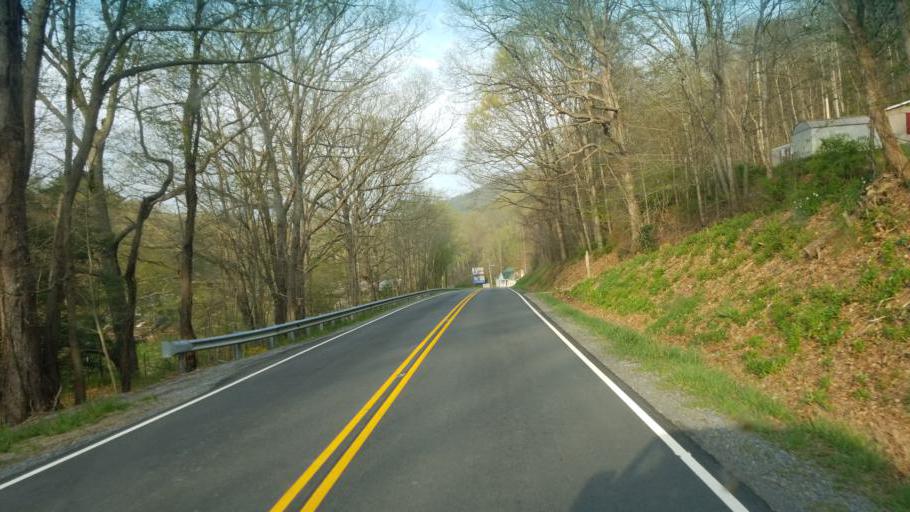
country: US
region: Virginia
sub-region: Smyth County
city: Marion
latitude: 36.8141
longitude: -81.4563
